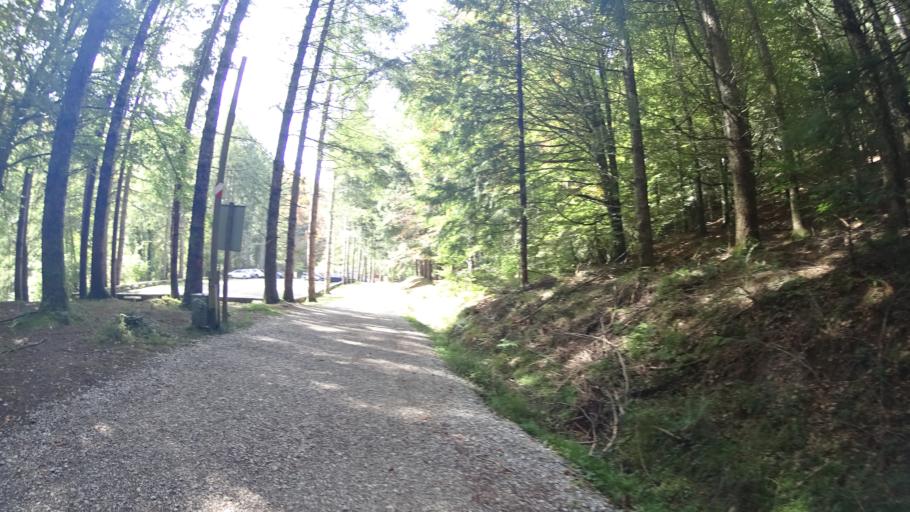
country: ES
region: Navarre
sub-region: Provincia de Navarra
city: Oronz
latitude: 42.9898
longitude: -1.1060
